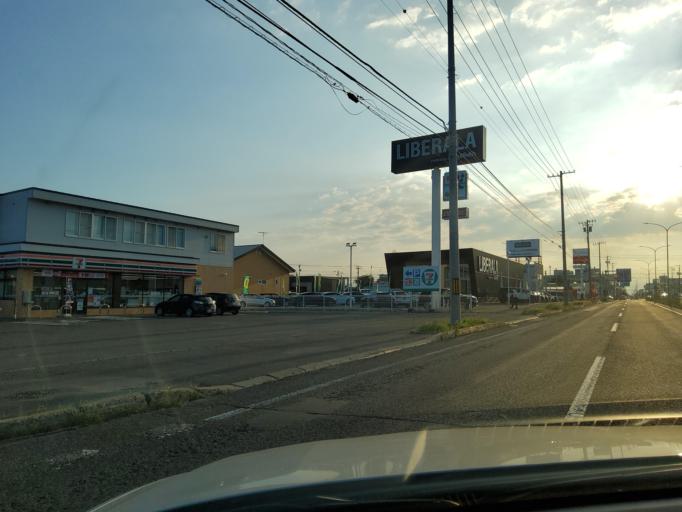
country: JP
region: Hokkaido
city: Obihiro
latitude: 42.9309
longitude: 143.1881
